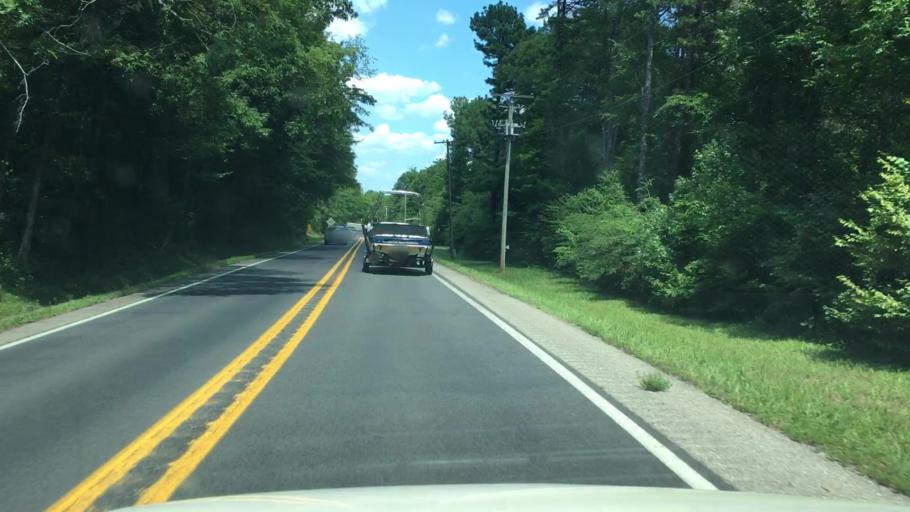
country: US
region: Arkansas
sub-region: Garland County
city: Lake Hamilton
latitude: 34.3852
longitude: -93.1265
